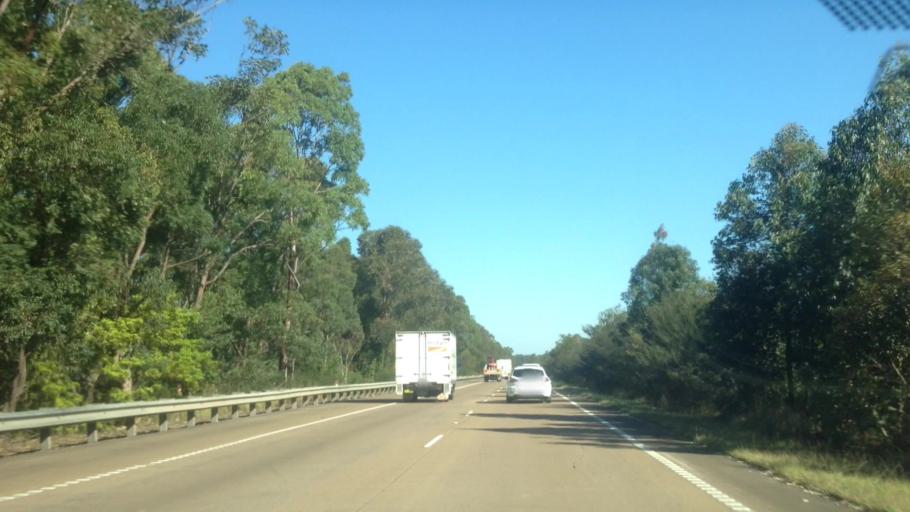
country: AU
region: New South Wales
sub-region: Wyong Shire
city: Charmhaven
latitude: -33.1579
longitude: 151.4705
